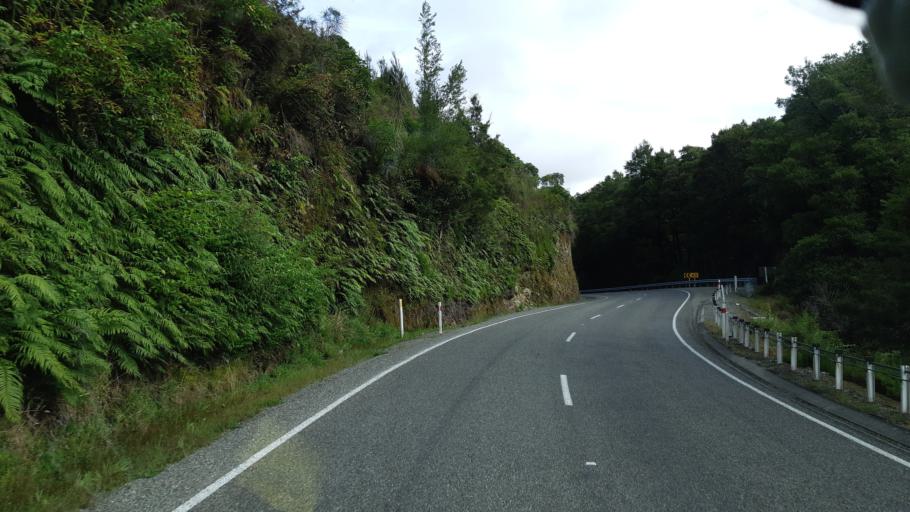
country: NZ
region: West Coast
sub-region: Buller District
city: Westport
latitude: -41.9864
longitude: 172.2095
